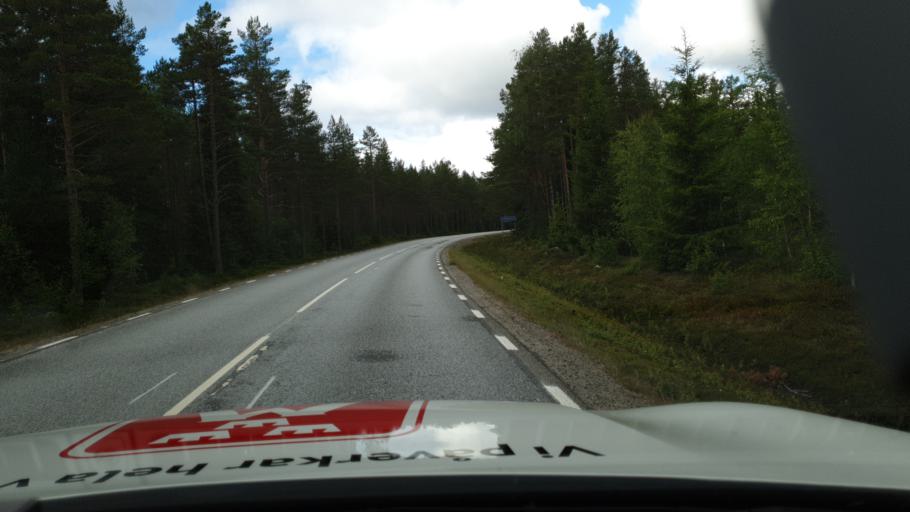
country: SE
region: Vaesterbotten
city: Obbola
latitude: 63.6747
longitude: 20.1949
